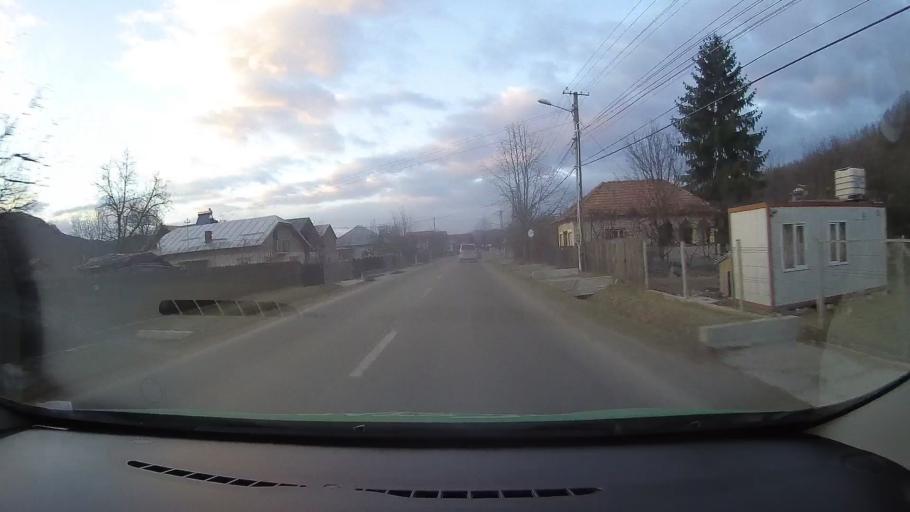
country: RO
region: Dambovita
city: Iedera de Jos
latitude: 45.0217
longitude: 25.6366
